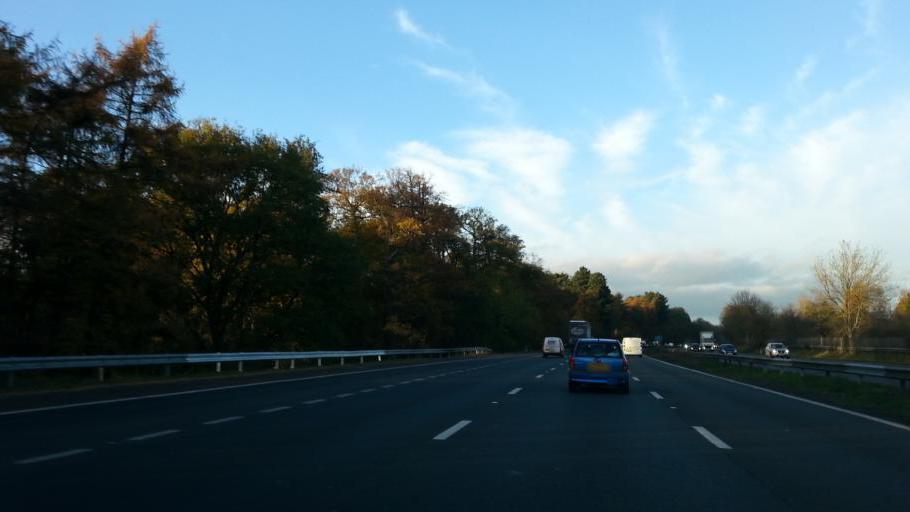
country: GB
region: England
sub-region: Hertfordshire
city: Welwyn Garden City
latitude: 51.8032
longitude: -0.2284
